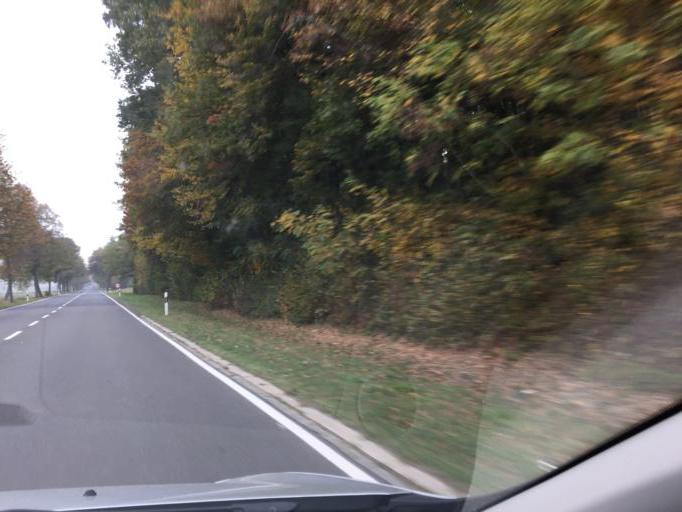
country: LU
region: Grevenmacher
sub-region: Canton de Remich
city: Waldbredimus
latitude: 49.5614
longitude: 6.3031
